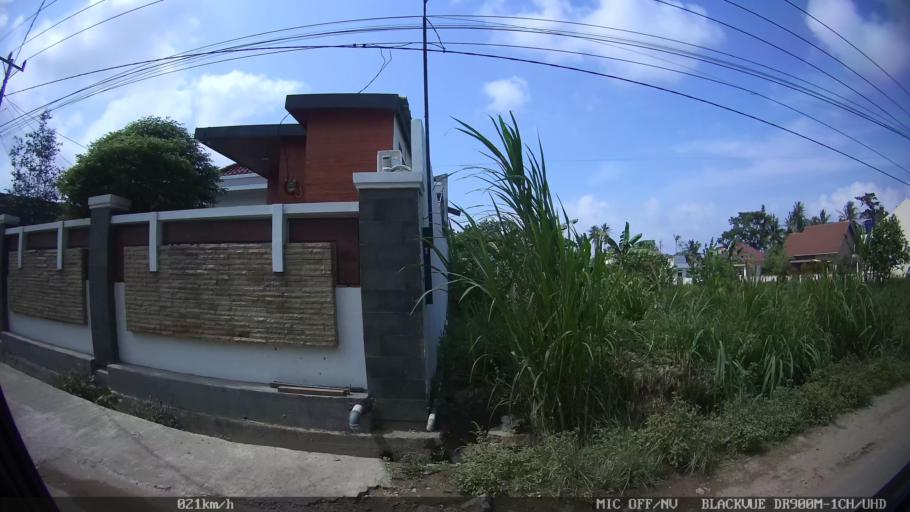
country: ID
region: Lampung
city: Kedaton
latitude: -5.3419
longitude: 105.2884
